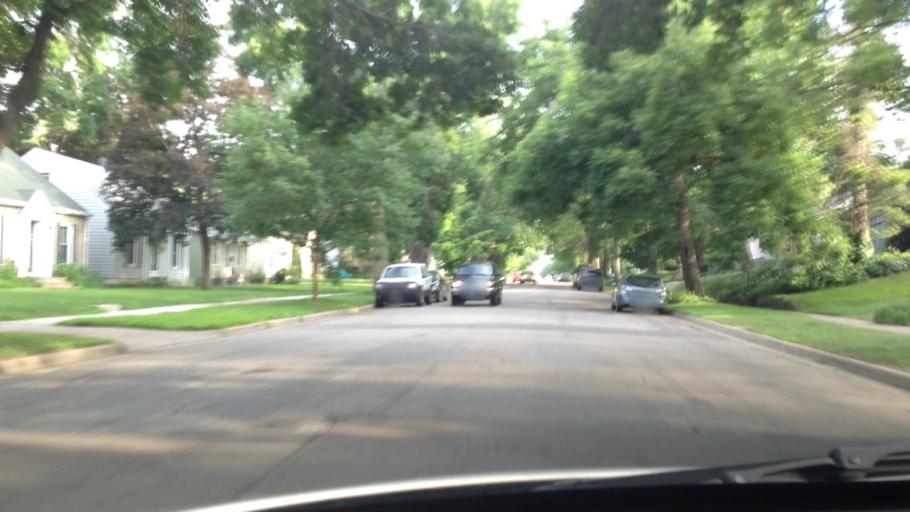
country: US
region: Minnesota
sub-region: Hennepin County
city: Saint Louis Park
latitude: 44.9528
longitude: -93.3607
